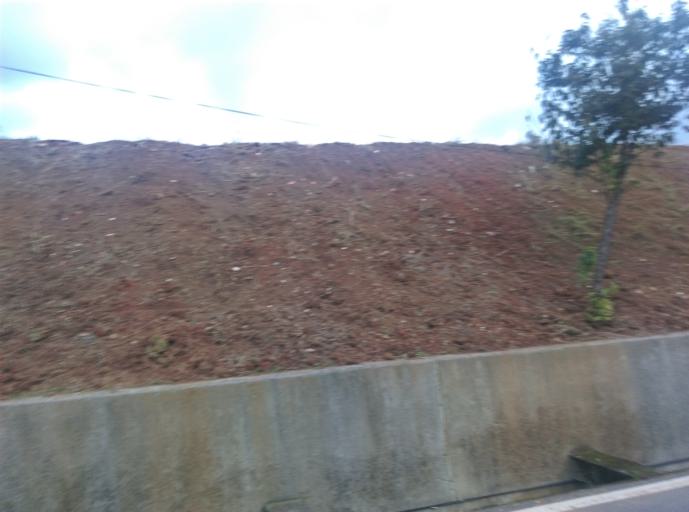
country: TW
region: Taiwan
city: Taoyuan City
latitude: 24.9977
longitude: 121.2509
